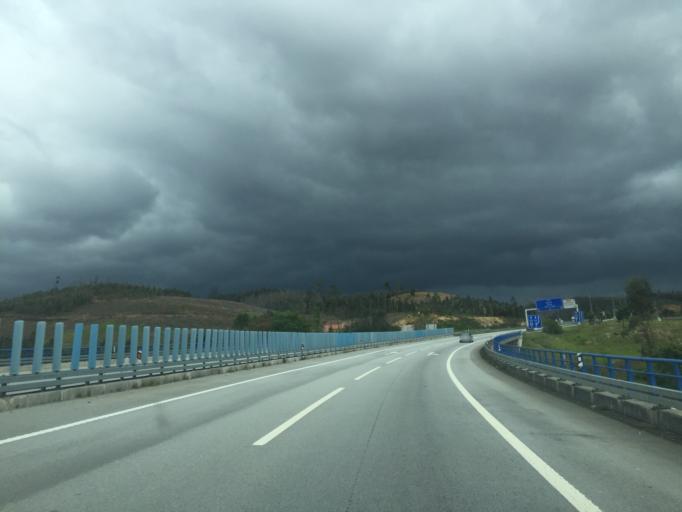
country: PT
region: Aveiro
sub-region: Albergaria-A-Velha
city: Albergaria-a-Velha
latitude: 40.6783
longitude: -8.4386
